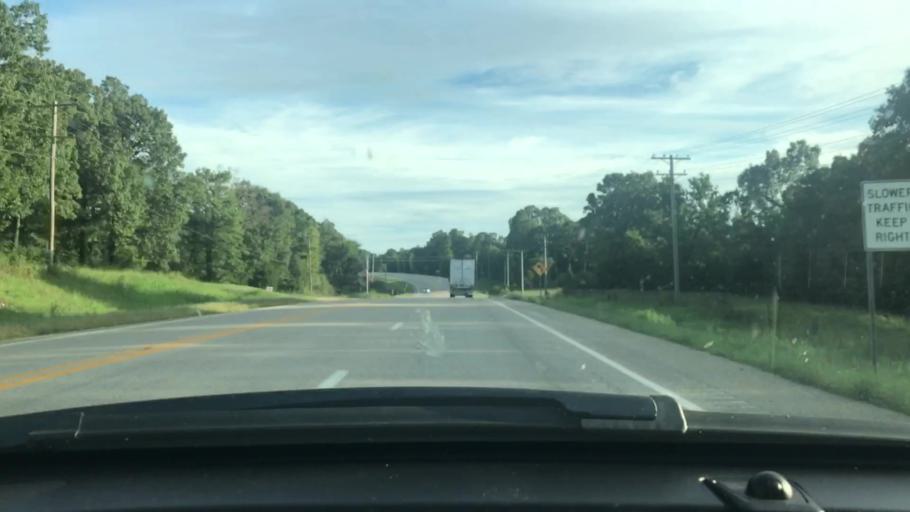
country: US
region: Arkansas
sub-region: Lawrence County
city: Hoxie
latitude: 36.1336
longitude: -91.1583
